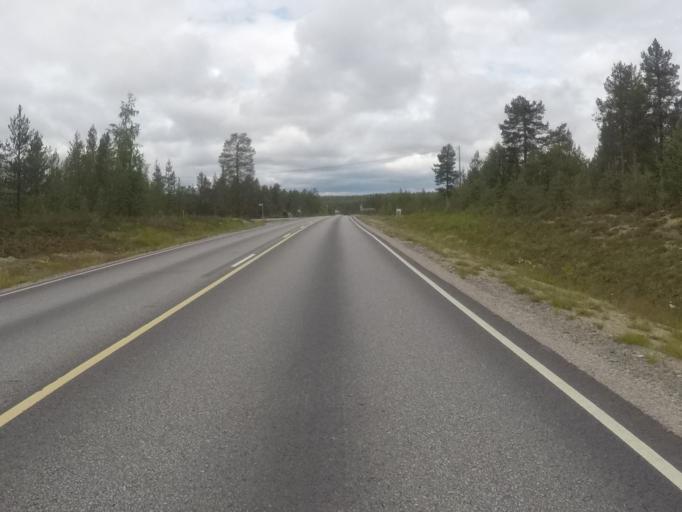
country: FI
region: Lapland
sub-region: Tunturi-Lappi
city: Muonio
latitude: 67.9850
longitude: 23.6474
